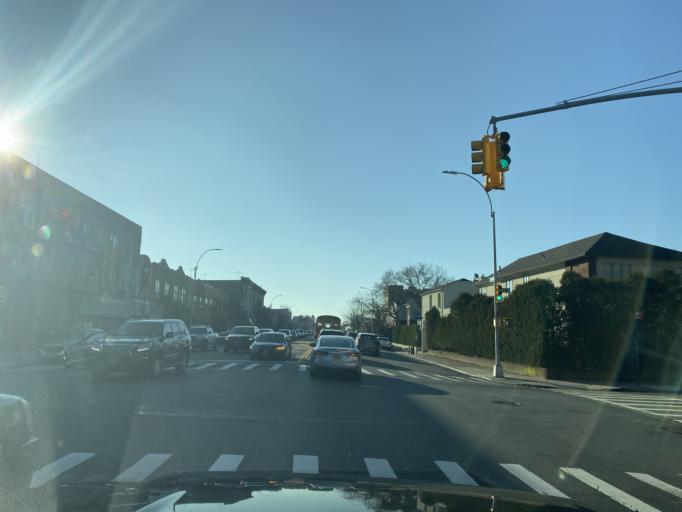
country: US
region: New York
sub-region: Kings County
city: Bensonhurst
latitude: 40.6056
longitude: -73.9618
